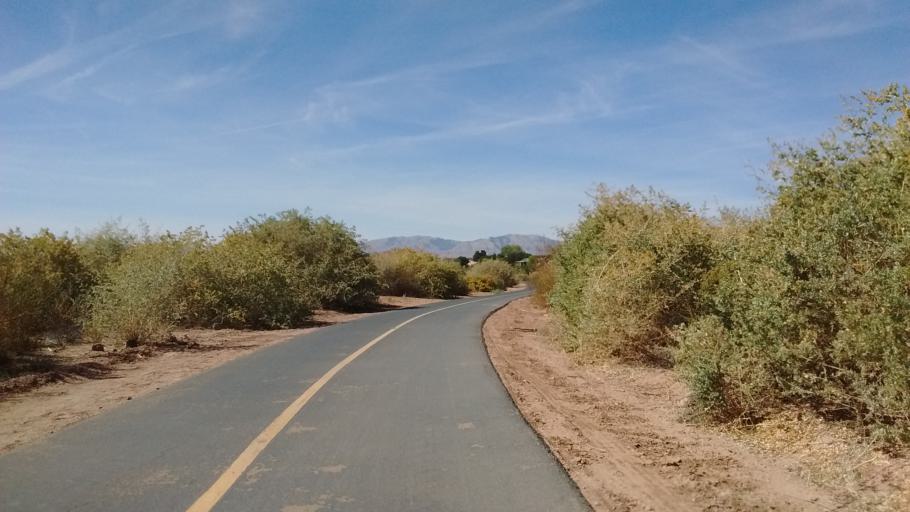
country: US
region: Utah
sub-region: Washington County
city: Saint George
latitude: 37.0877
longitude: -113.5490
